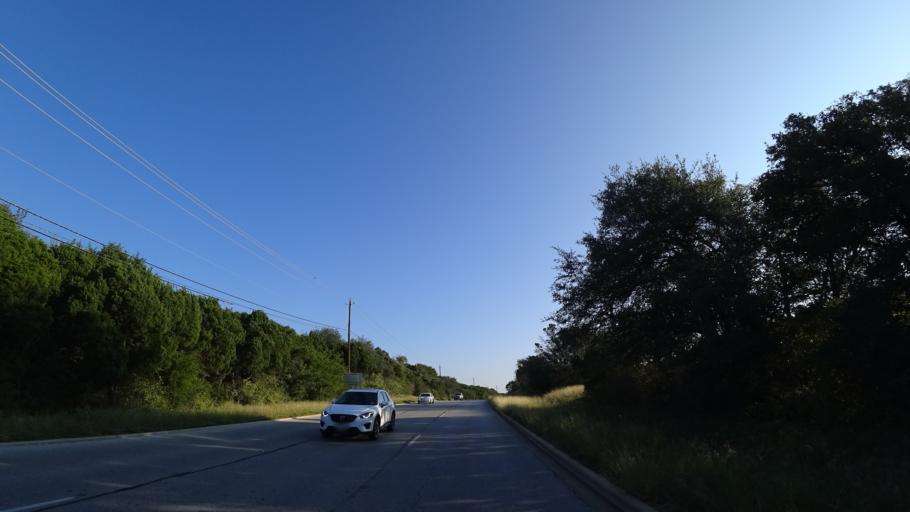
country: US
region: Texas
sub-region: Travis County
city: Rollingwood
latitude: 30.2534
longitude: -97.8055
